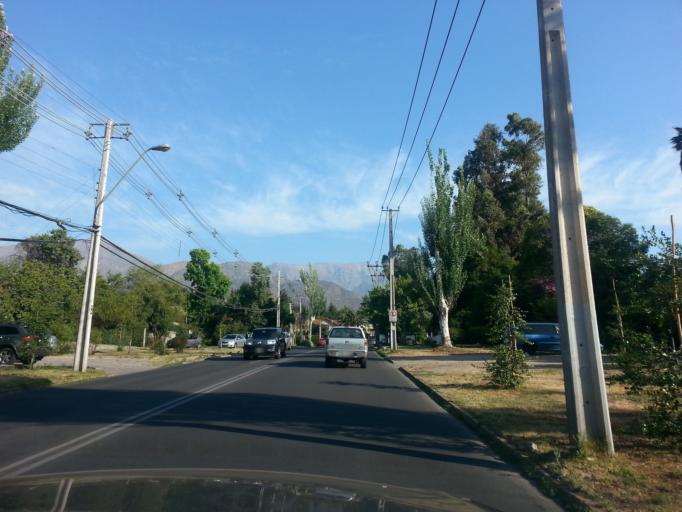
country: CL
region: Santiago Metropolitan
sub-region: Provincia de Santiago
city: Villa Presidente Frei, Nunoa, Santiago, Chile
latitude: -33.3898
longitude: -70.5267
